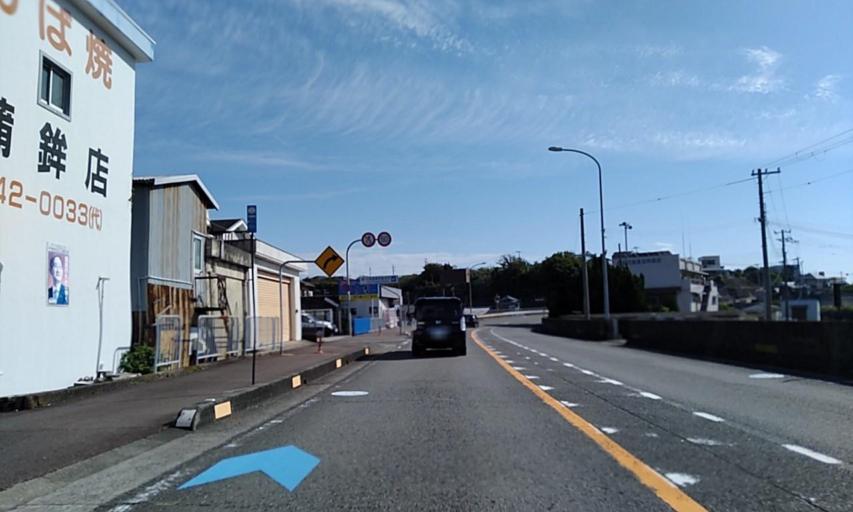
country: JP
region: Wakayama
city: Gobo
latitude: 33.8132
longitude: 135.2187
